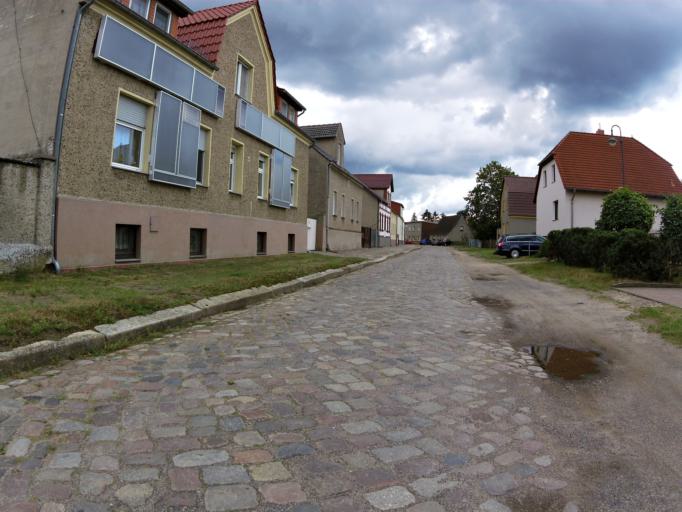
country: DE
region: Brandenburg
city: Storkow
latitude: 52.2549
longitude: 13.9209
